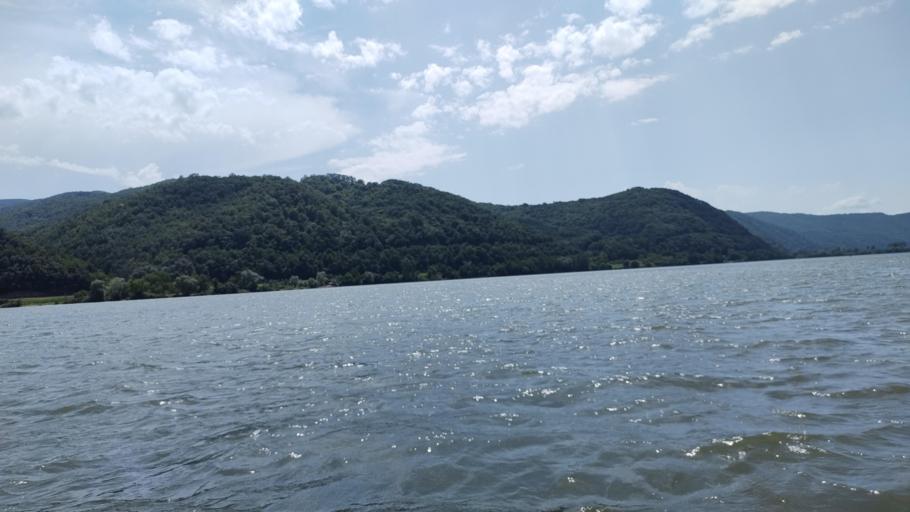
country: RO
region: Caras-Severin
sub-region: Comuna Berzasca
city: Liubcova
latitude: 44.6507
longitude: 21.8695
